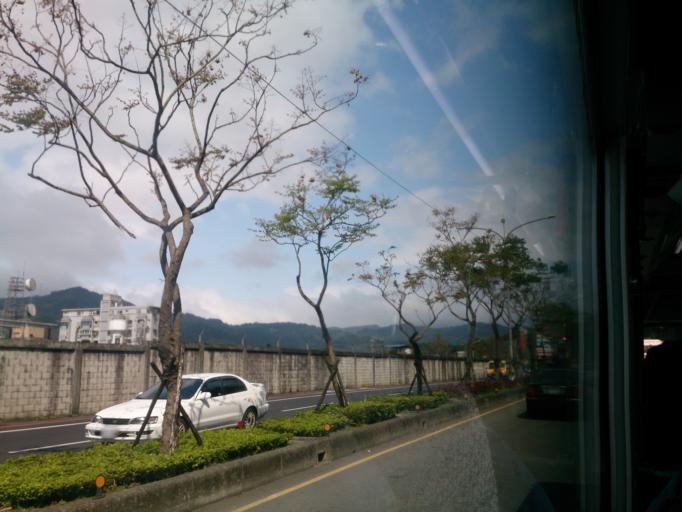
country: TW
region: Taipei
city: Taipei
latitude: 25.0015
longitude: 121.6254
